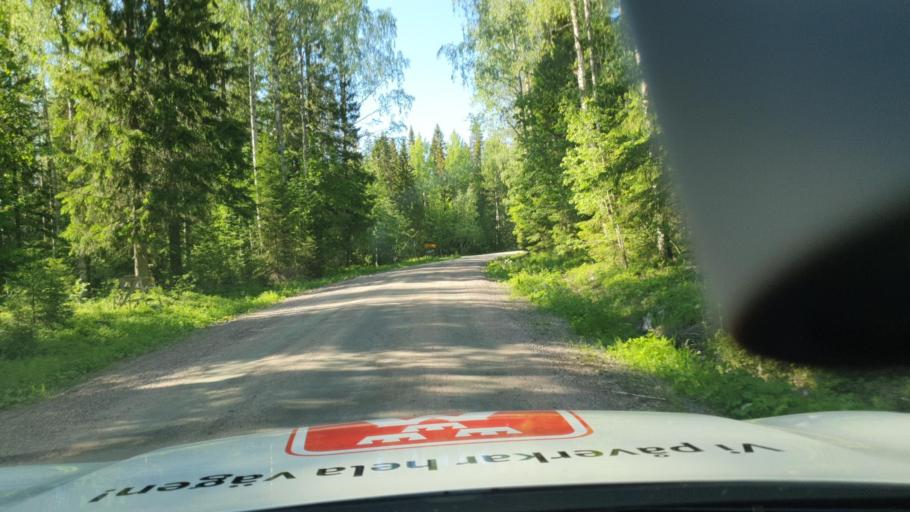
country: SE
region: Vaesterbotten
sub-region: Vannas Kommun
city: Vaennaes
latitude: 63.7869
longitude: 19.6251
